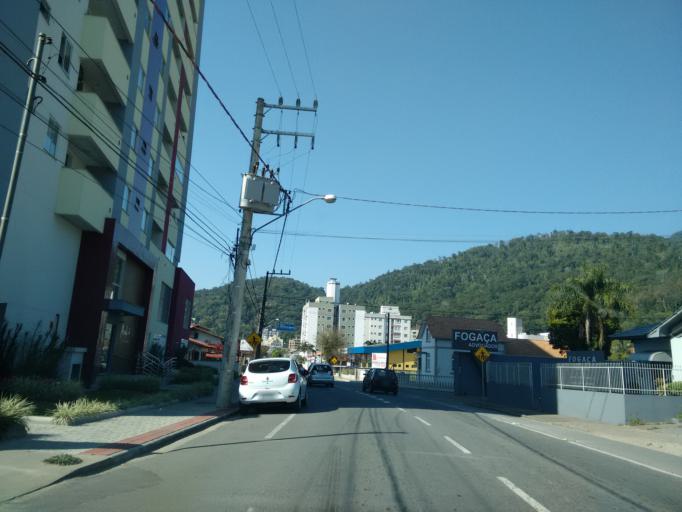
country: BR
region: Santa Catarina
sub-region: Jaragua Do Sul
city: Jaragua do Sul
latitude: -26.5005
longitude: -49.0860
